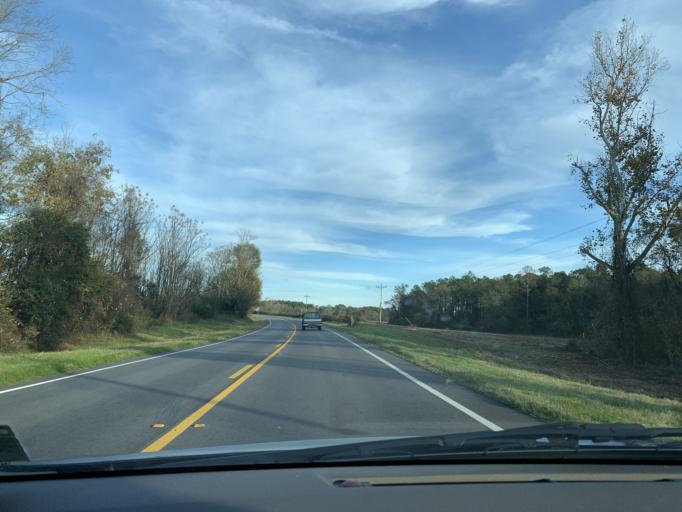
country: US
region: Georgia
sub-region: Irwin County
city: Ocilla
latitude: 31.5921
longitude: -83.2036
